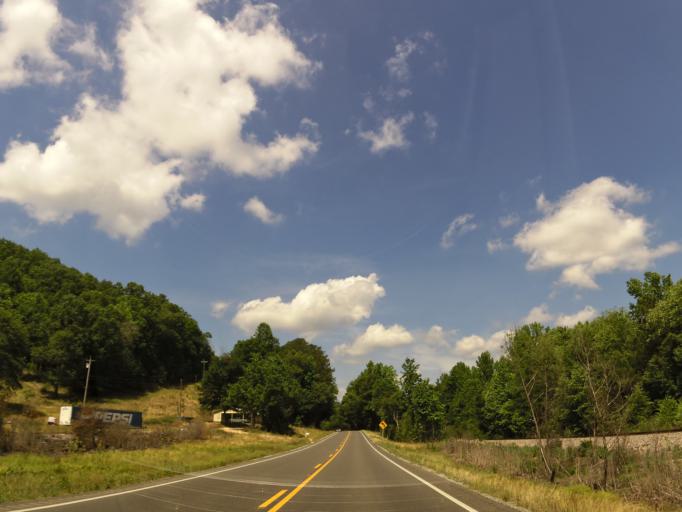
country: US
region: Alabama
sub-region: Marion County
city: Guin
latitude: 33.9548
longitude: -87.9602
